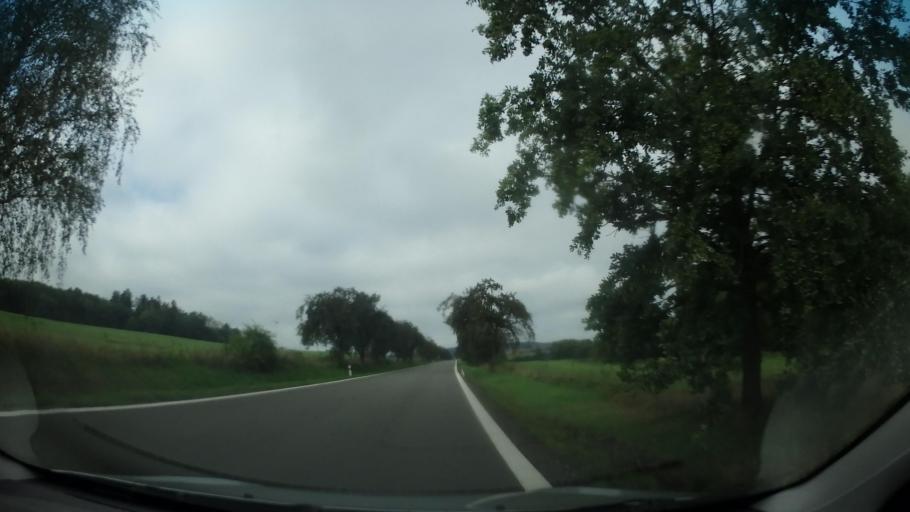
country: CZ
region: Central Bohemia
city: Neveklov
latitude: 49.7534
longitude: 14.5978
